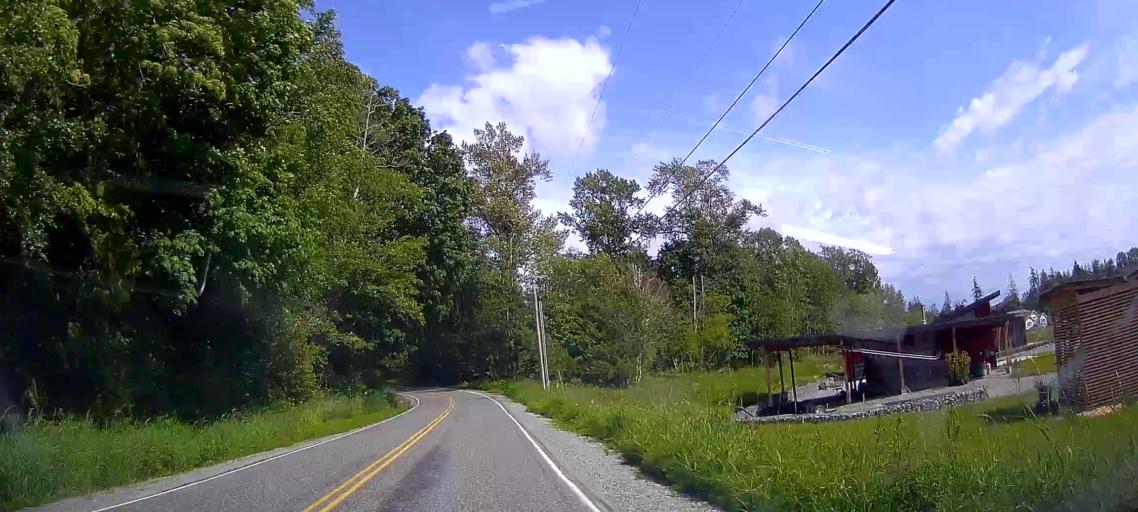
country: US
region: Washington
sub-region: Skagit County
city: Burlington
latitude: 48.5706
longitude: -122.3912
